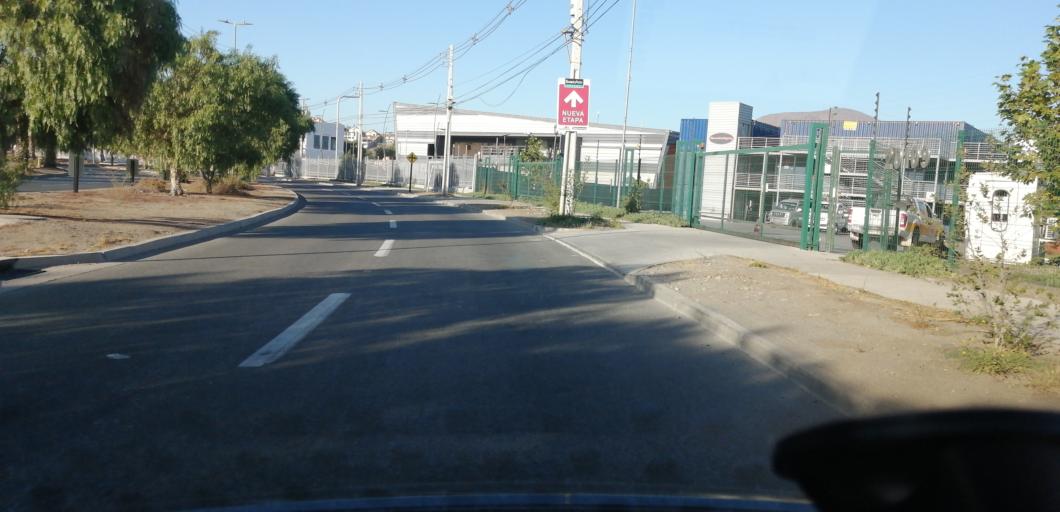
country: CL
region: Santiago Metropolitan
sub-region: Provincia de Santiago
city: Lo Prado
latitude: -33.4499
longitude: -70.8501
